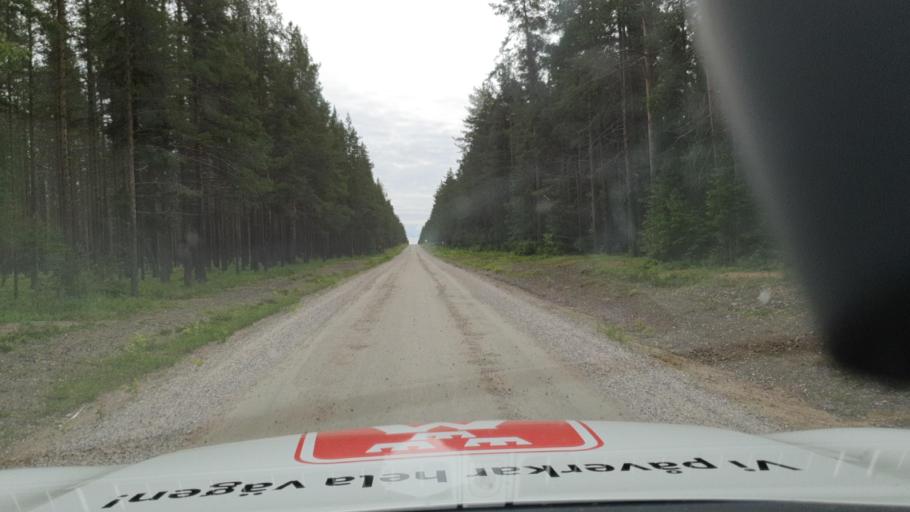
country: SE
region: Vaesterbotten
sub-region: Skelleftea Kommun
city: Forsbacka
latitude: 64.6519
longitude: 20.4442
